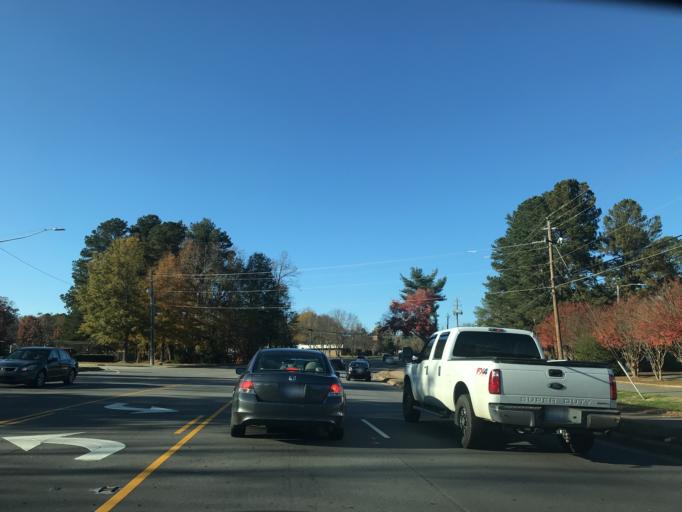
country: US
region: North Carolina
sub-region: Wake County
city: West Raleigh
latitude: 35.8603
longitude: -78.6184
